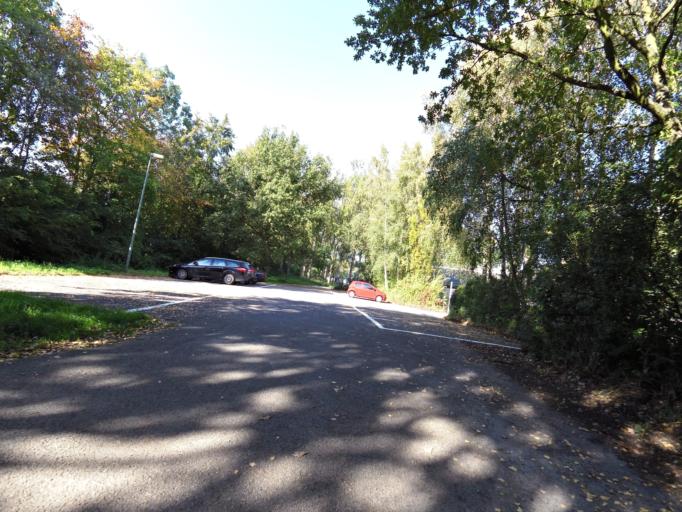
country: NL
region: South Holland
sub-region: Gemeente Vlaardingen
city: Vlaardingen
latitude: 51.9263
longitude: 4.3373
